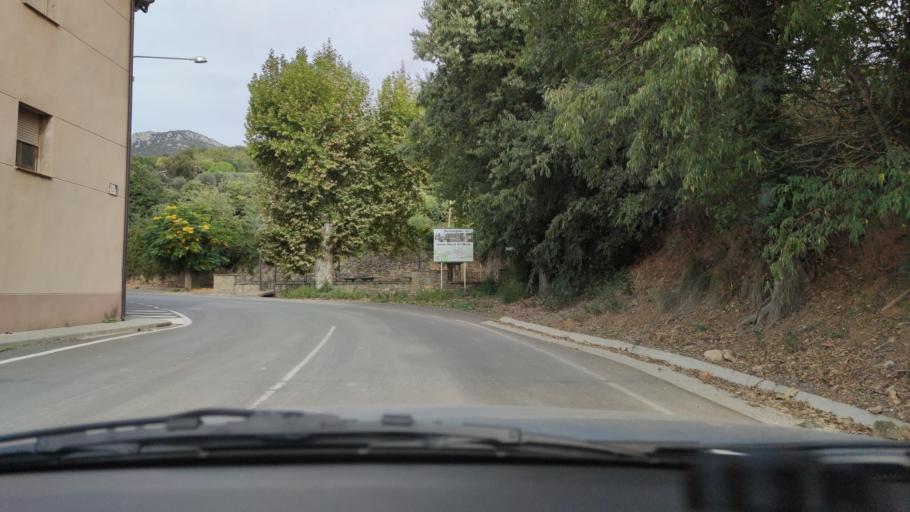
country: ES
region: Catalonia
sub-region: Provincia de Lleida
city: Artesa de Segre
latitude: 41.9927
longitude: 0.9972
